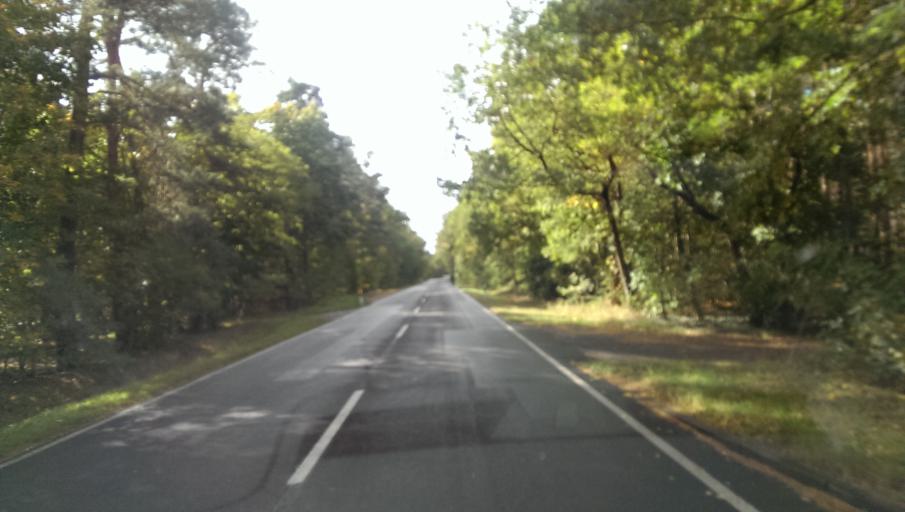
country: DE
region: Brandenburg
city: Luckenwalde
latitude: 52.0521
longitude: 13.1385
